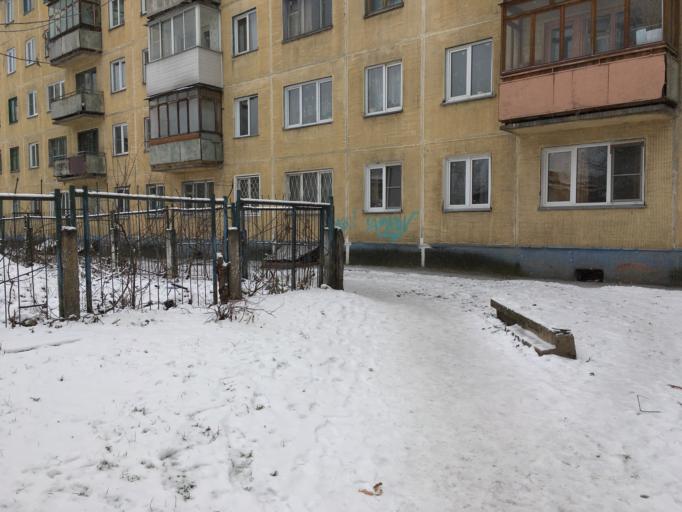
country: RU
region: Novosibirsk
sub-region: Novosibirskiy Rayon
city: Novosibirsk
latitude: 55.0540
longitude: 82.9671
